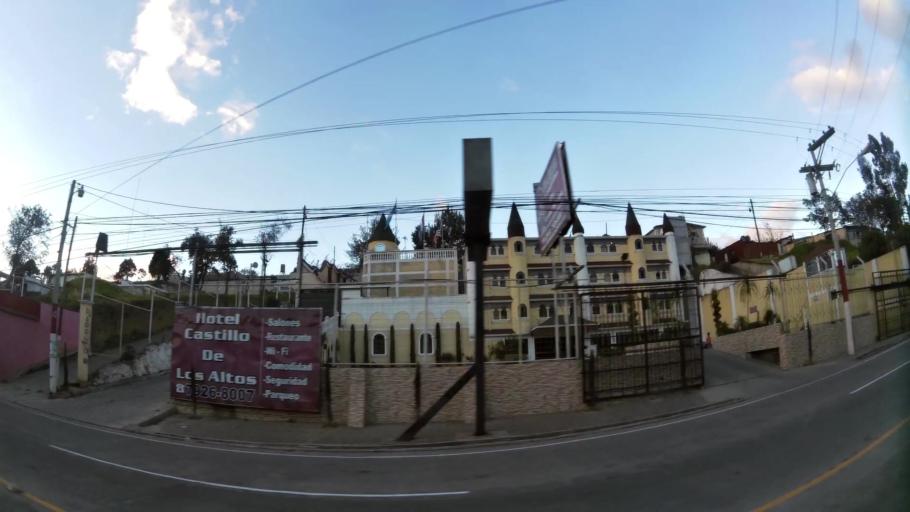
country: GT
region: Quetzaltenango
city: Almolonga
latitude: 14.8491
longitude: -91.4780
